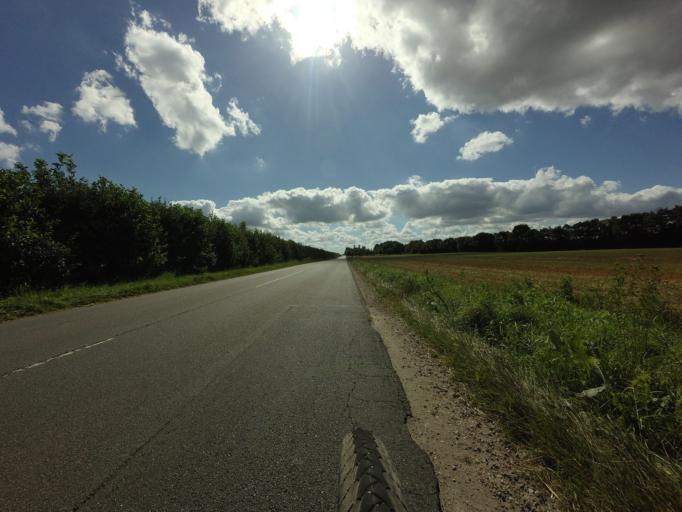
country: DK
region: Central Jutland
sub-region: Ikast-Brande Kommune
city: Brande
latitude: 55.9780
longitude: 9.1437
